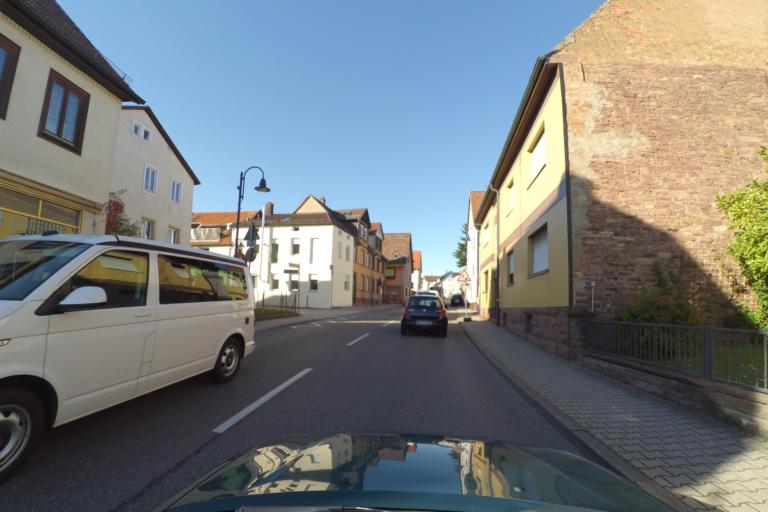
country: DE
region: Baden-Wuerttemberg
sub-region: Karlsruhe Region
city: Pforzheim
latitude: 48.8564
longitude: 8.6944
